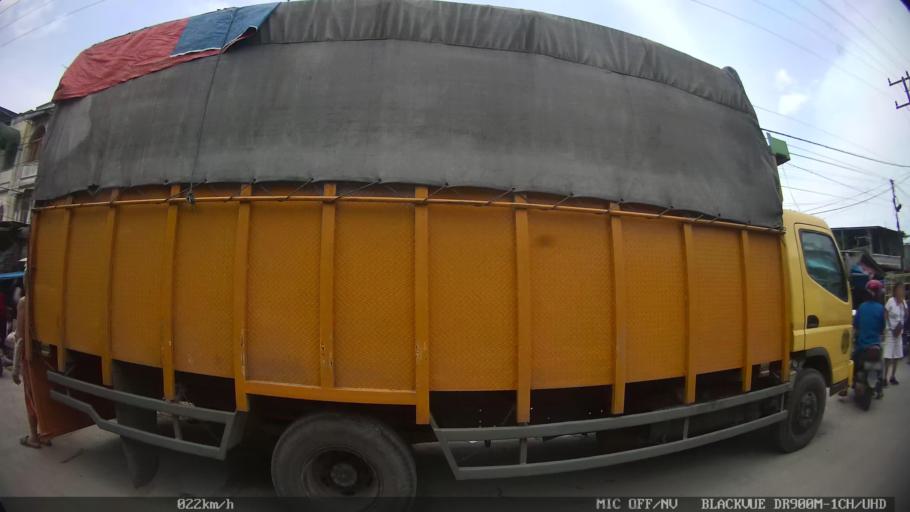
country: ID
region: North Sumatra
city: Labuhan Deli
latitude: 3.7099
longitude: 98.6618
